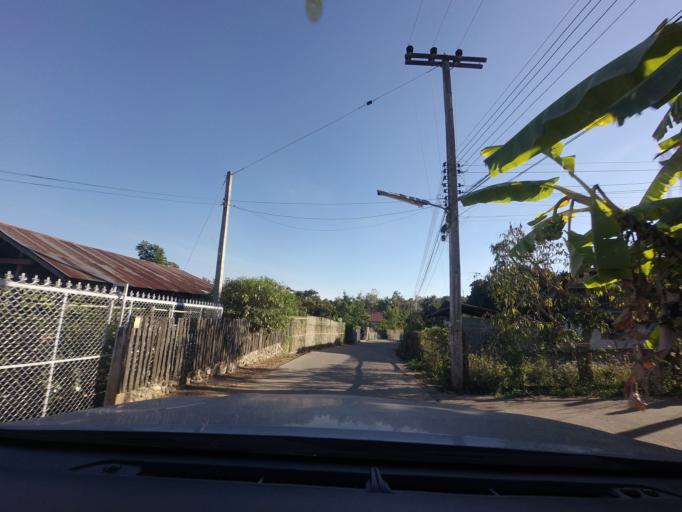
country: TH
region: Mae Hong Son
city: Wiang Nuea
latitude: 19.3928
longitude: 98.4222
